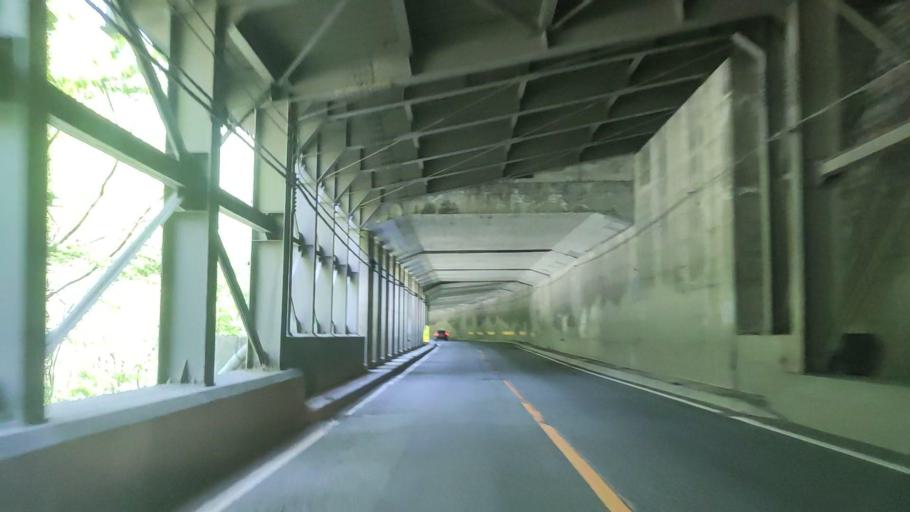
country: JP
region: Niigata
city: Itoigawa
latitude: 36.9057
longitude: 137.8643
